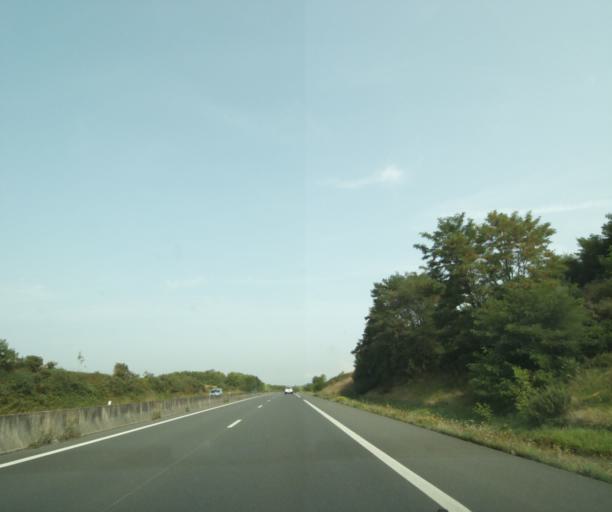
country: FR
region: Pays de la Loire
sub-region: Departement de la Sarthe
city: Champfleur
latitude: 48.3434
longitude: 0.1005
